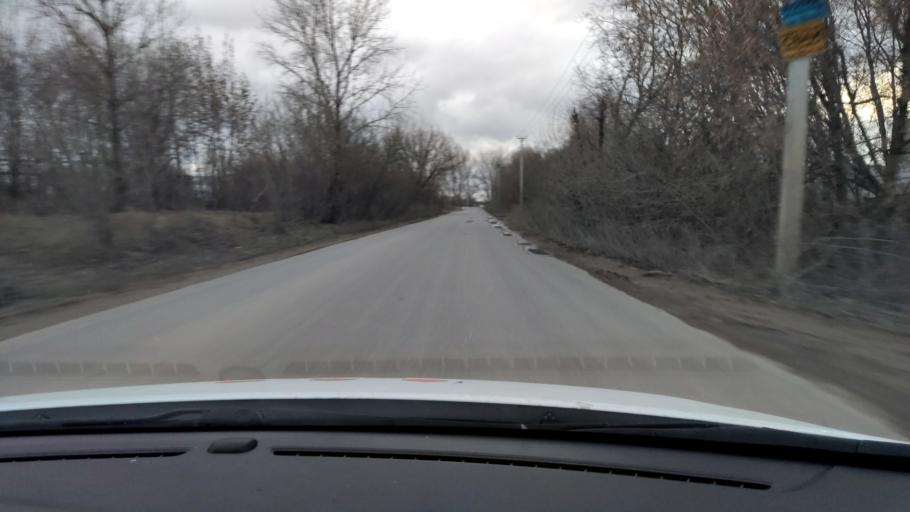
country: RU
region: Tatarstan
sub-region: Gorod Kazan'
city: Kazan
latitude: 55.7257
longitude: 49.0972
